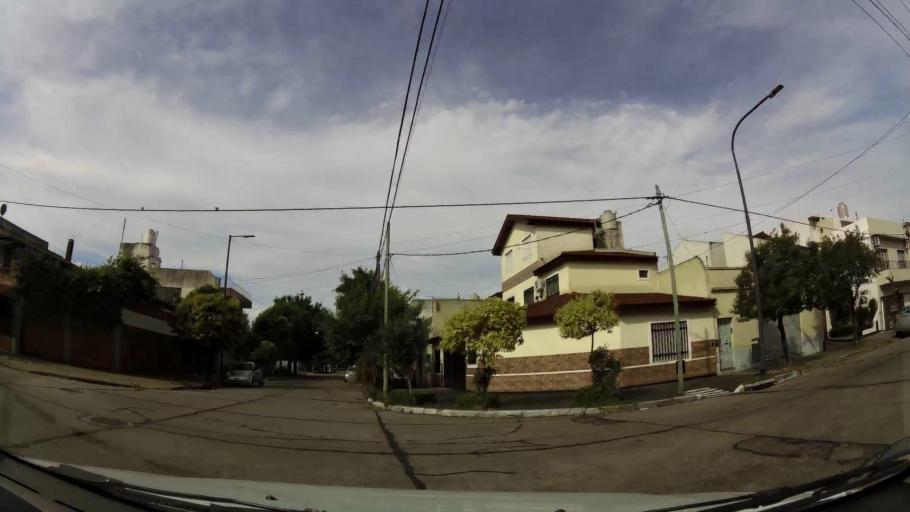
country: AR
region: Buenos Aires F.D.
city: Villa Lugano
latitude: -34.6557
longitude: -58.4790
